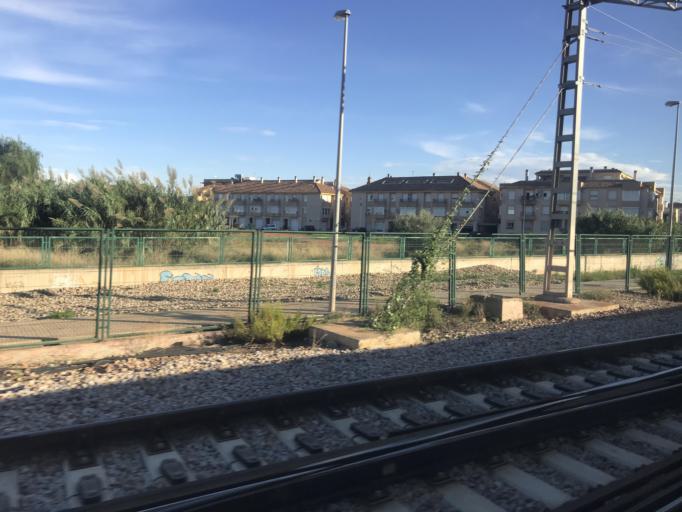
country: ES
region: Valencia
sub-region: Provincia de Valencia
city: Pucol
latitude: 39.6203
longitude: -0.3029
